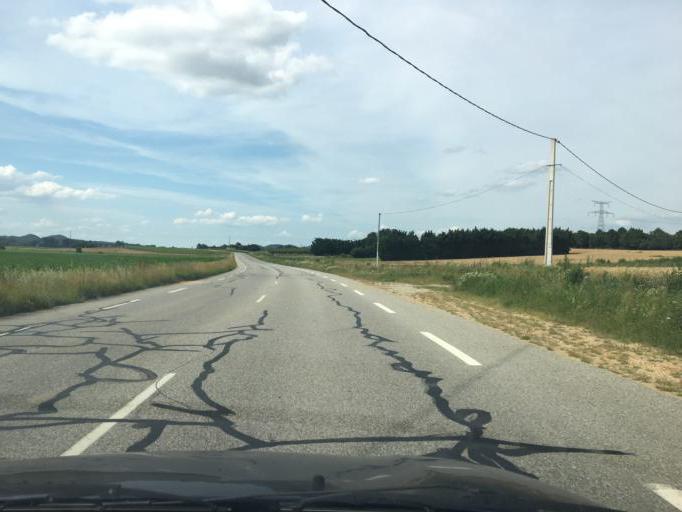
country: FR
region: Rhone-Alpes
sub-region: Departement de la Drome
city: Clerieux
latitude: 45.0811
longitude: 4.9376
